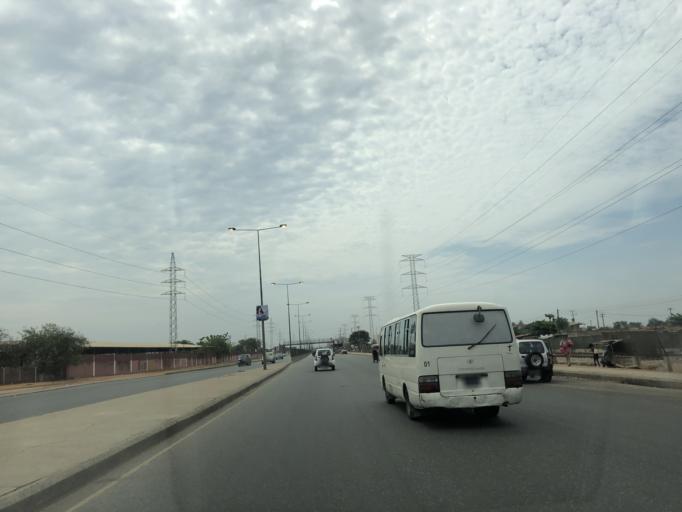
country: AO
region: Luanda
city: Luanda
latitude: -8.8604
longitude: 13.3042
